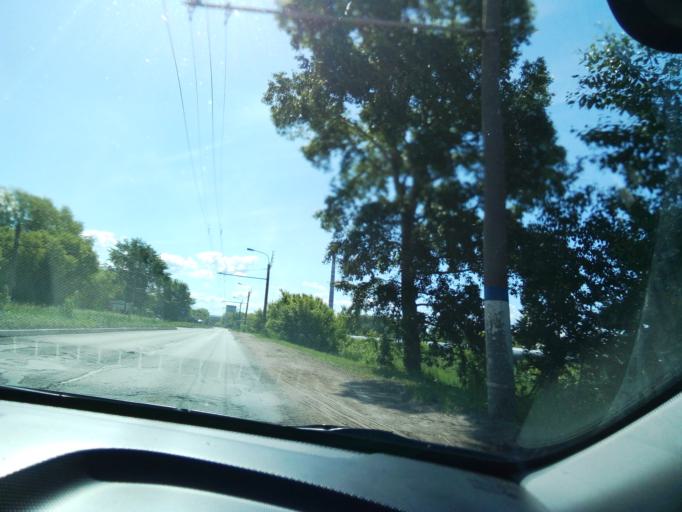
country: RU
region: Chuvashia
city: Novocheboksarsk
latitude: 56.0930
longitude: 47.4974
